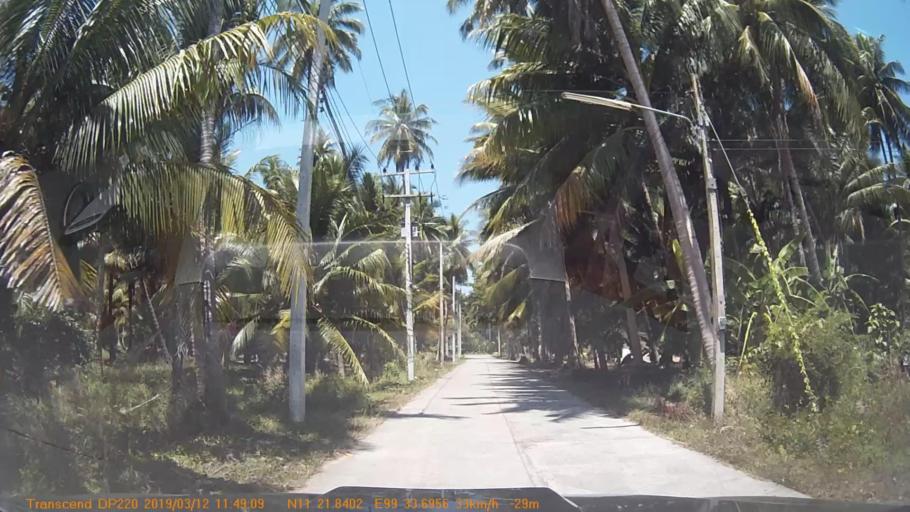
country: TH
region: Prachuap Khiri Khan
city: Thap Sakae
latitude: 11.3641
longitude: 99.5615
